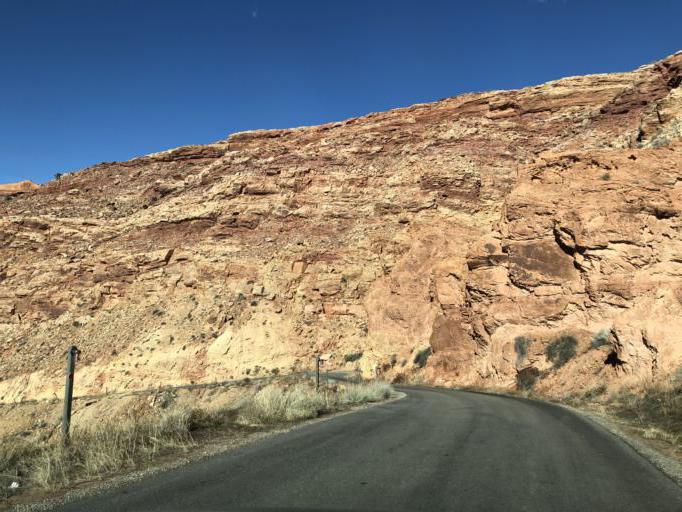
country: US
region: Utah
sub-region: Grand County
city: Moab
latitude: 38.5876
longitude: -109.5553
